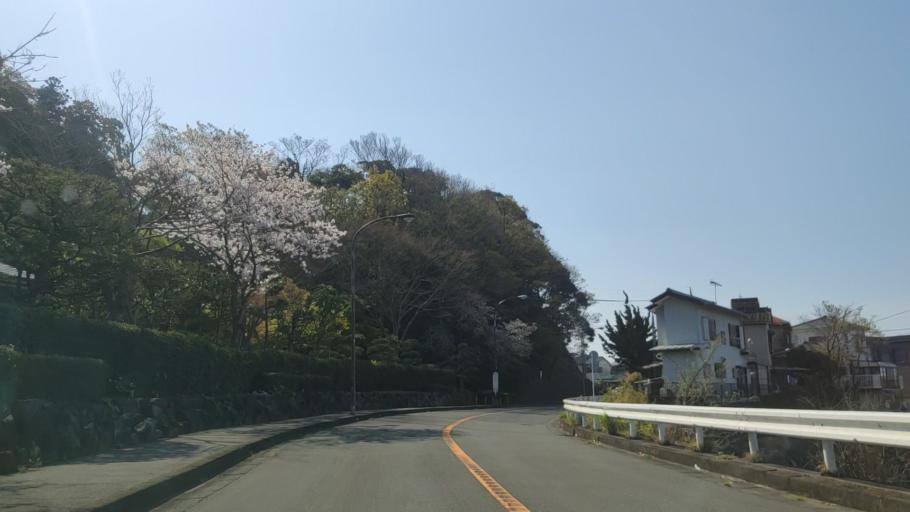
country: JP
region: Kanagawa
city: Oiso
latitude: 35.3061
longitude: 139.2890
